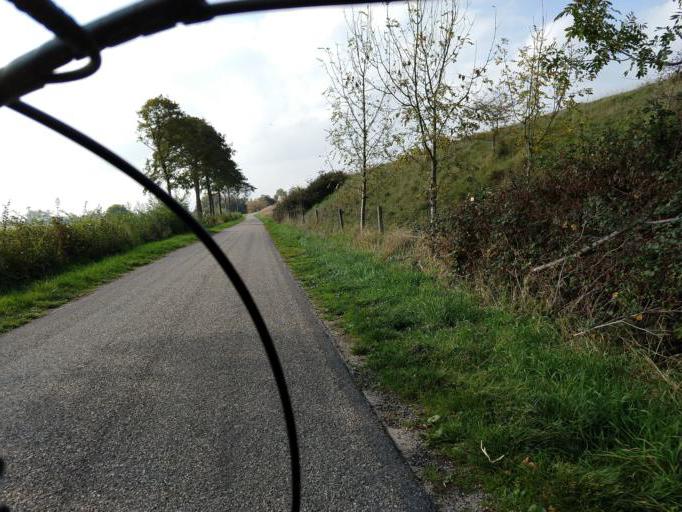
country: NL
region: Zeeland
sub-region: Schouwen-Duiveland
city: Bruinisse
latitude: 51.6769
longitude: 4.0258
